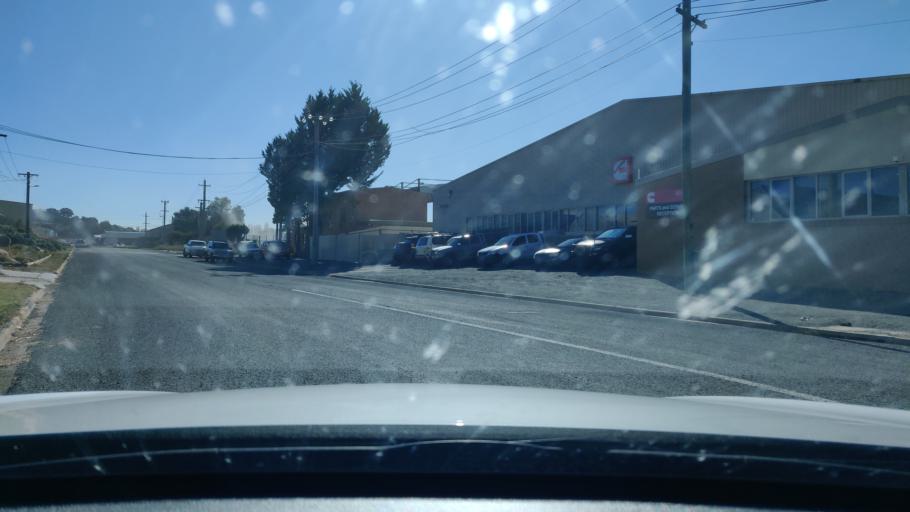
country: AU
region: Australian Capital Territory
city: Macarthur
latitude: -35.3882
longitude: 149.1747
